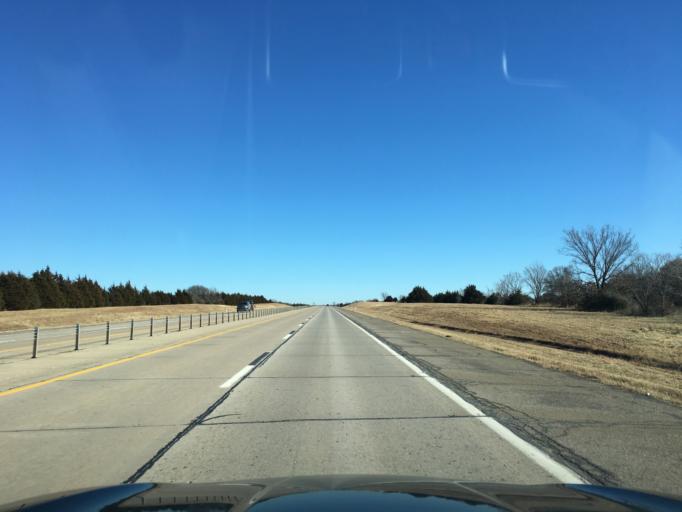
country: US
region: Oklahoma
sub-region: Pawnee County
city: Pawnee
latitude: 36.2249
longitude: -96.8338
